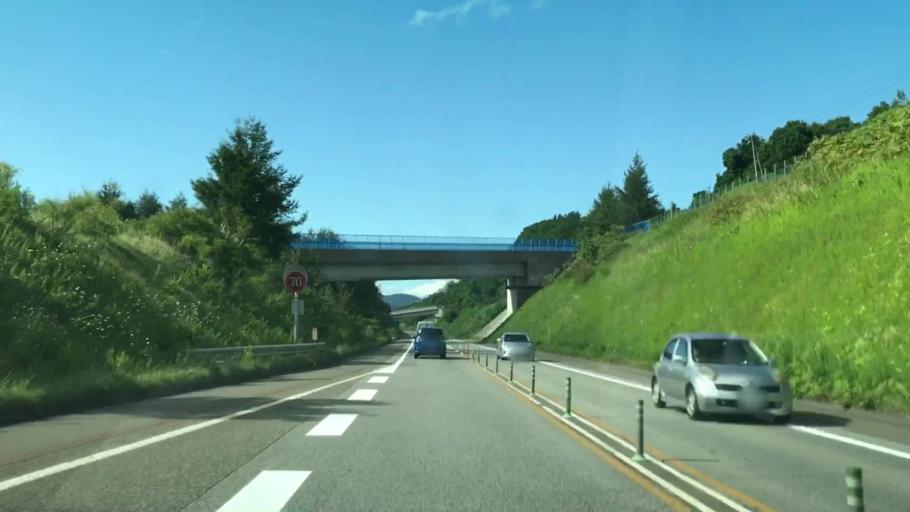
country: JP
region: Hokkaido
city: Date
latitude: 42.4697
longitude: 140.9066
